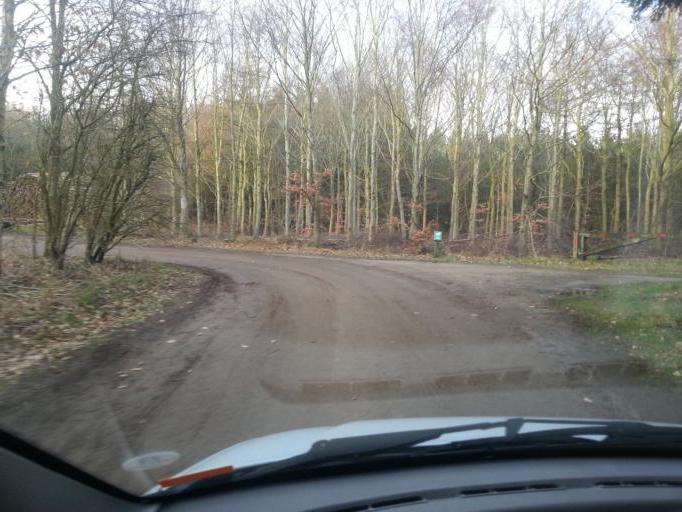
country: DK
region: South Denmark
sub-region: Esbjerg Kommune
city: Esbjerg
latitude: 55.4860
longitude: 8.5123
